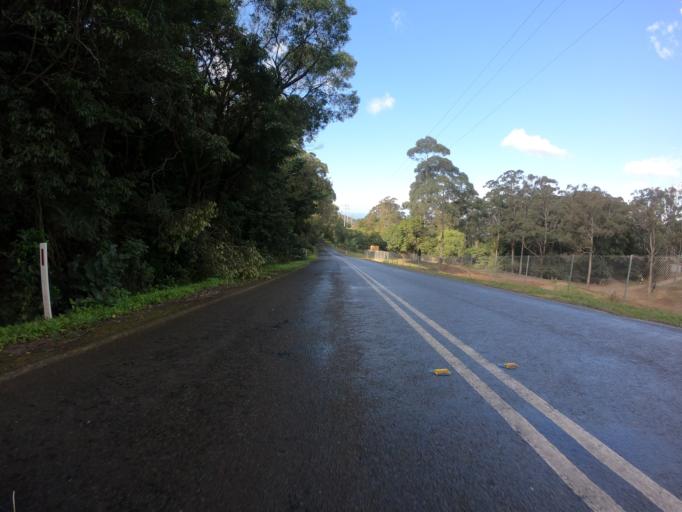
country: AU
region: New South Wales
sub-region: Wollongong
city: Cordeaux Heights
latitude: -34.4124
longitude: 150.8161
